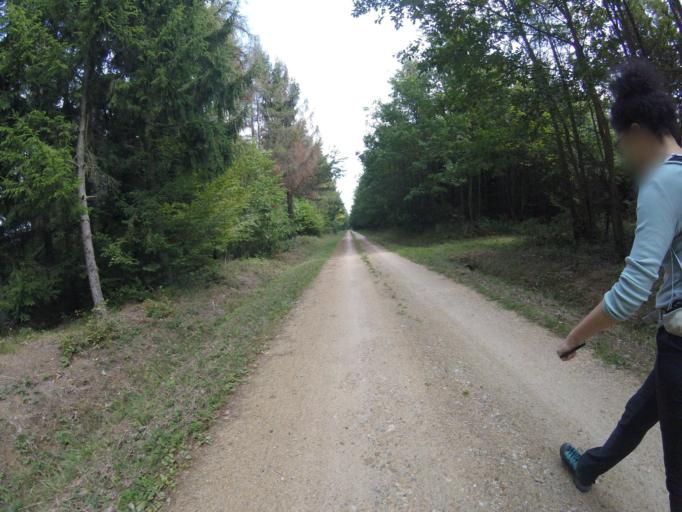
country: HU
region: Vas
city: Koszeg
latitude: 47.3722
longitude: 16.6111
